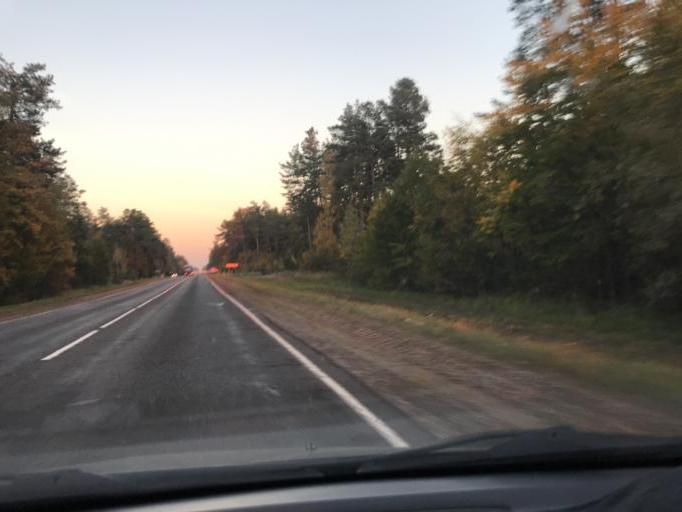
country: BY
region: Mogilev
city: Hlusha
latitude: 53.1026
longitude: 29.0369
